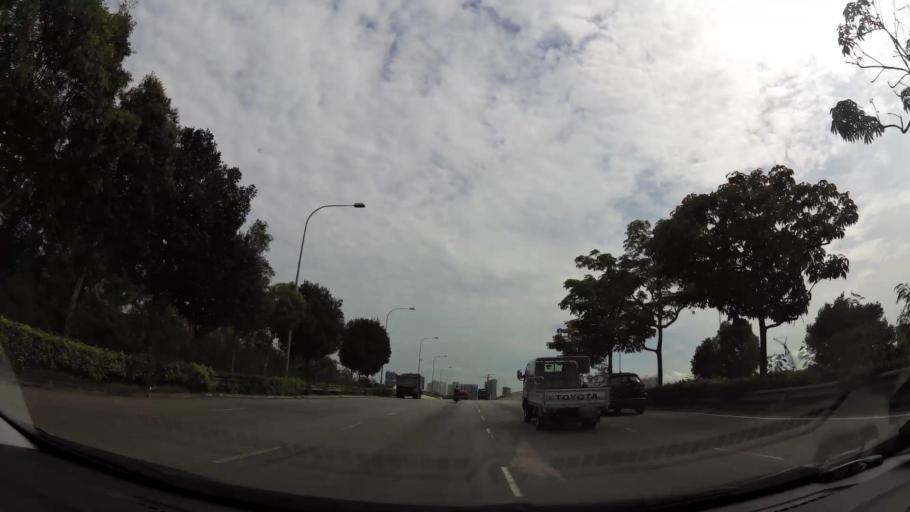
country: SG
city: Singapore
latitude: 1.3066
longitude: 103.7519
